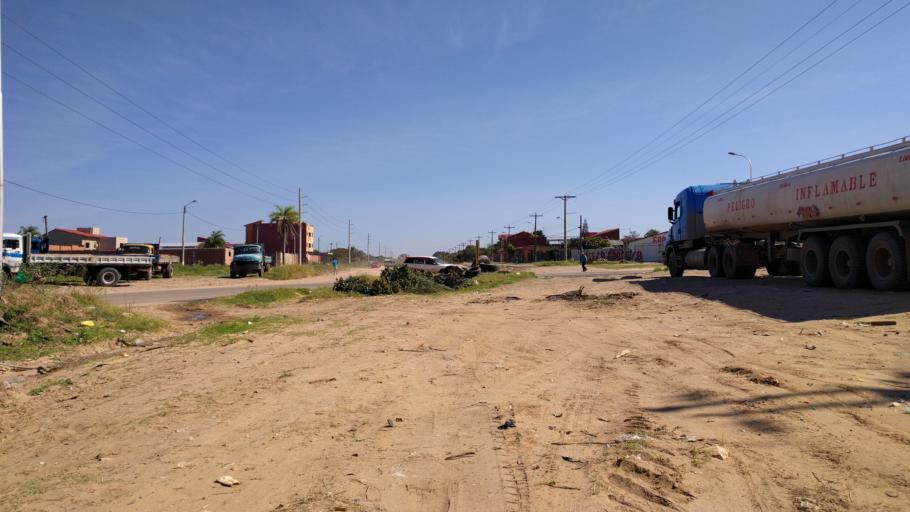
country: BO
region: Santa Cruz
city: Santa Cruz de la Sierra
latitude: -17.8659
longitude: -63.2020
